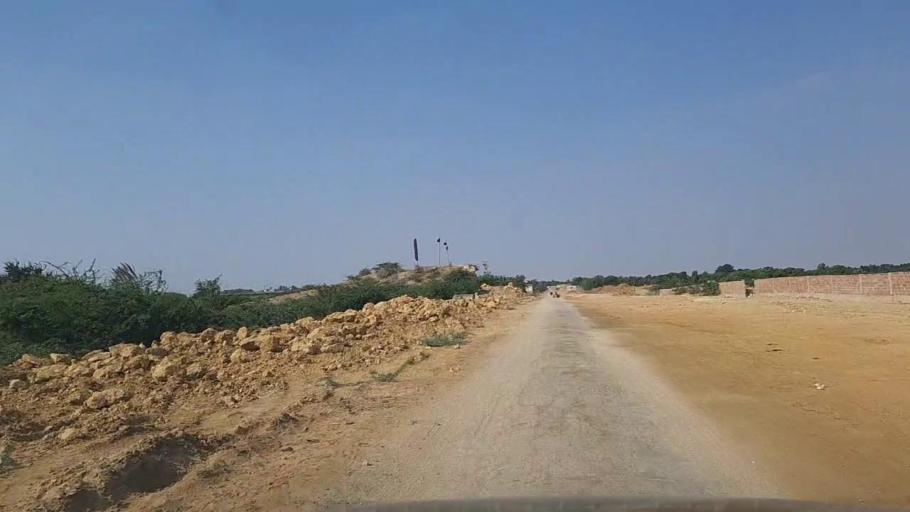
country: PK
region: Sindh
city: Gharo
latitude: 24.7599
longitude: 67.5789
